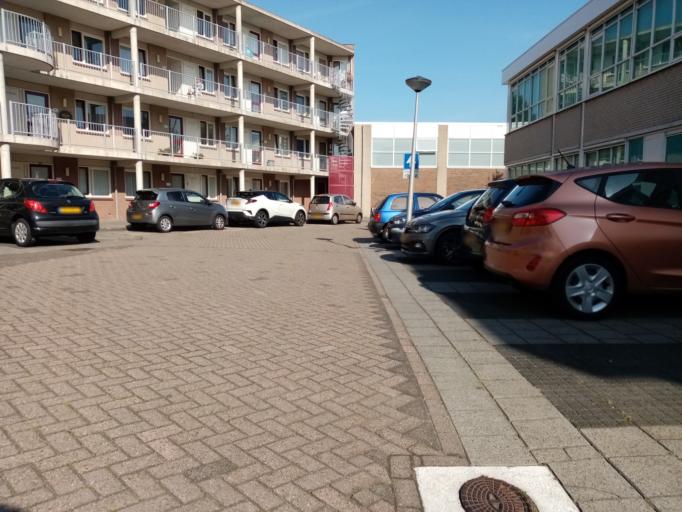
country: NL
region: South Holland
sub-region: Gemeente Noordwijk
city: Noordwijk-Binnen
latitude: 52.2306
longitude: 4.4400
